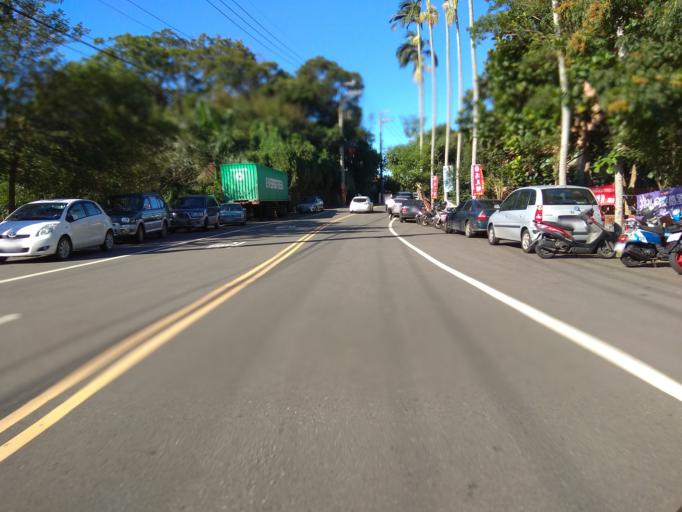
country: TW
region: Taiwan
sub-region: Hsinchu
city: Zhubei
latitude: 24.8466
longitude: 121.1175
